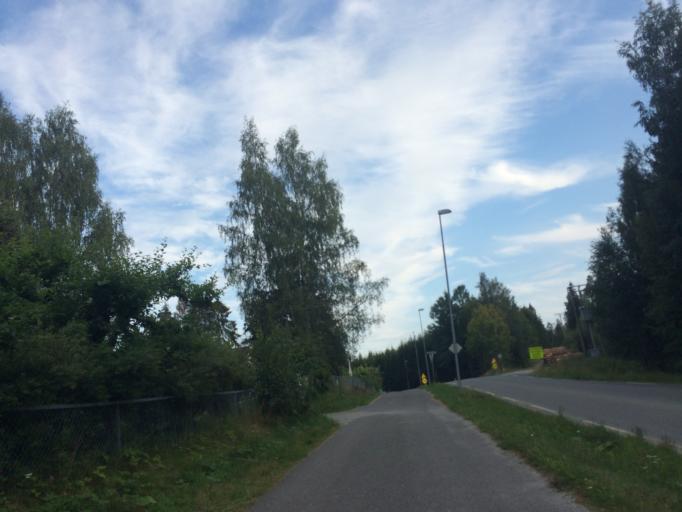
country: NO
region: Akershus
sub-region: Ski
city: Ski
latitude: 59.7003
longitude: 10.8458
